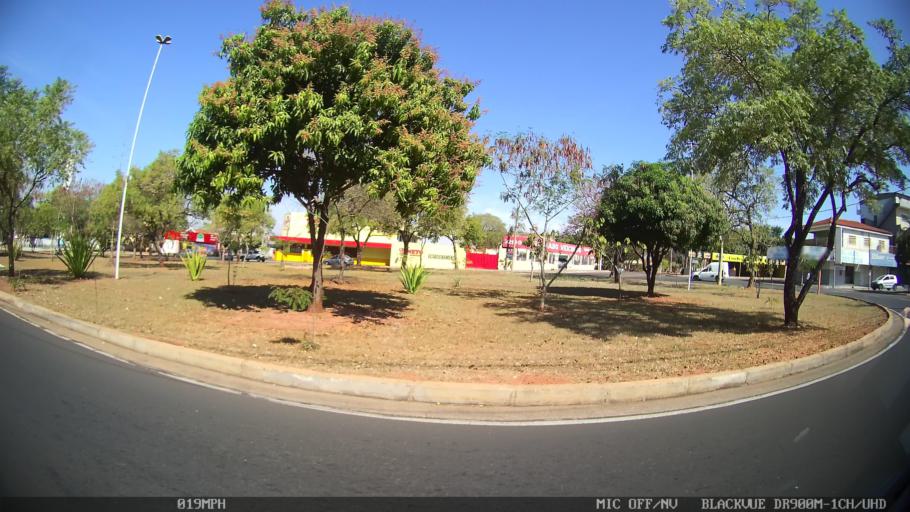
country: BR
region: Sao Paulo
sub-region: Sao Jose Do Rio Preto
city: Sao Jose do Rio Preto
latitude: -20.7850
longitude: -49.3921
